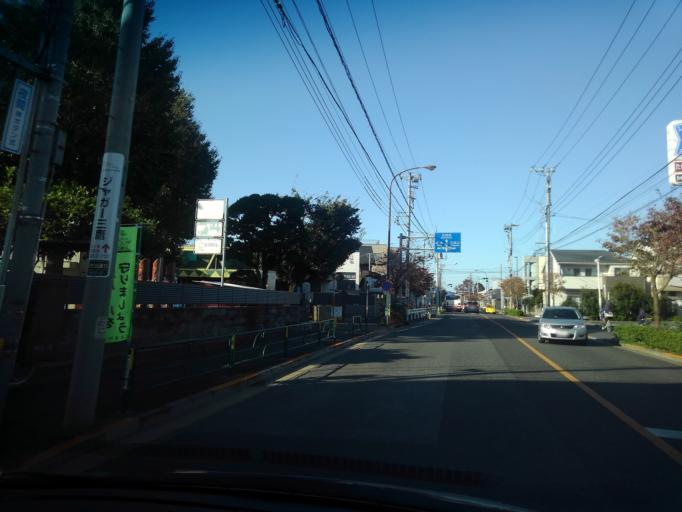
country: JP
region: Tokyo
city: Mitaka-shi
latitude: 35.6803
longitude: 139.5386
